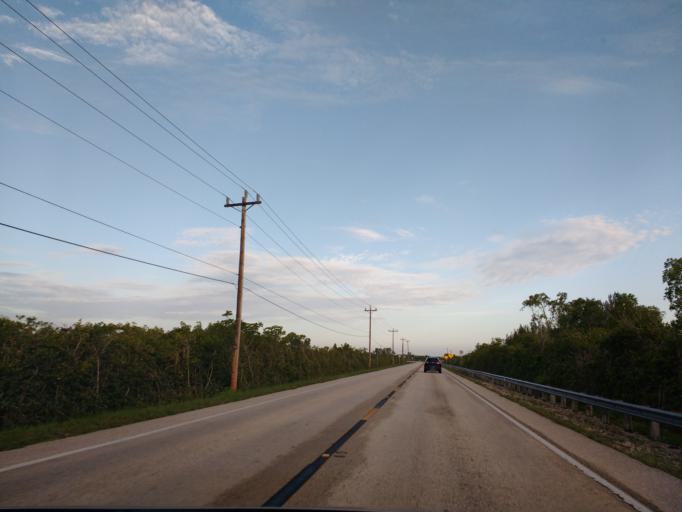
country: US
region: Florida
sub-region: Lee County
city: Pine Island Center
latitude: 26.6388
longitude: -82.0522
